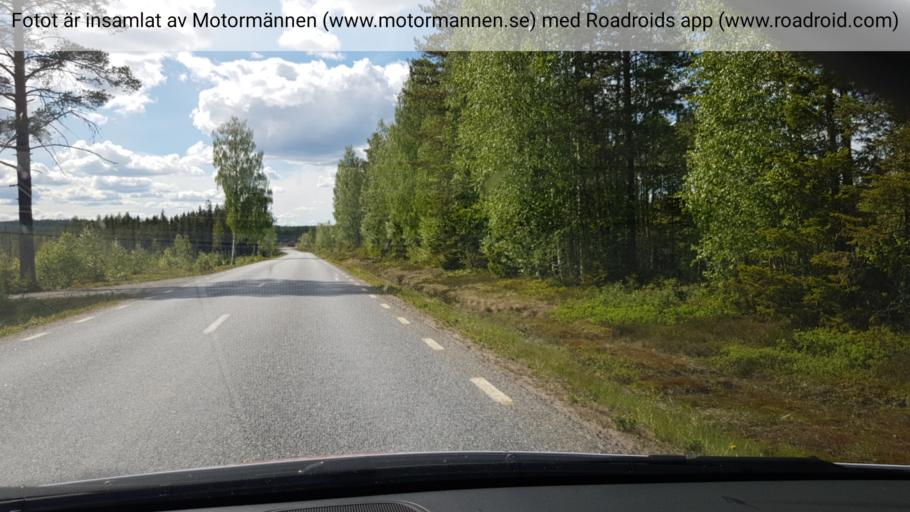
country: SE
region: Vaesterbotten
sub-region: Skelleftea Kommun
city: Burtraesk
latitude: 64.4018
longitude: 20.3609
